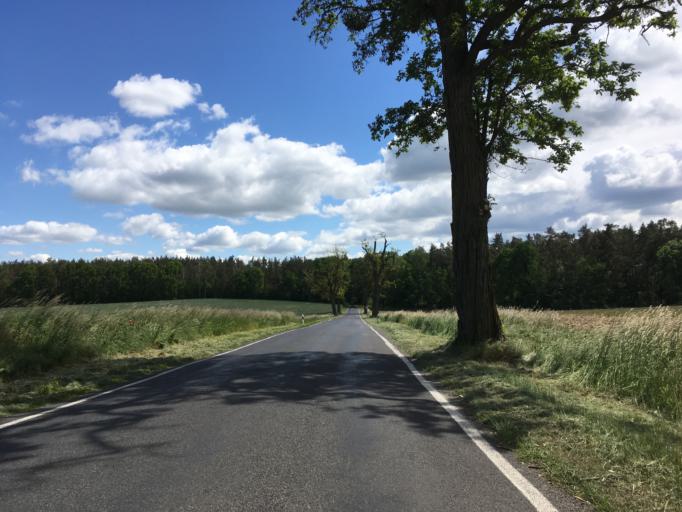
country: DE
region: Brandenburg
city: Protzel
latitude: 52.7013
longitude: 14.0192
